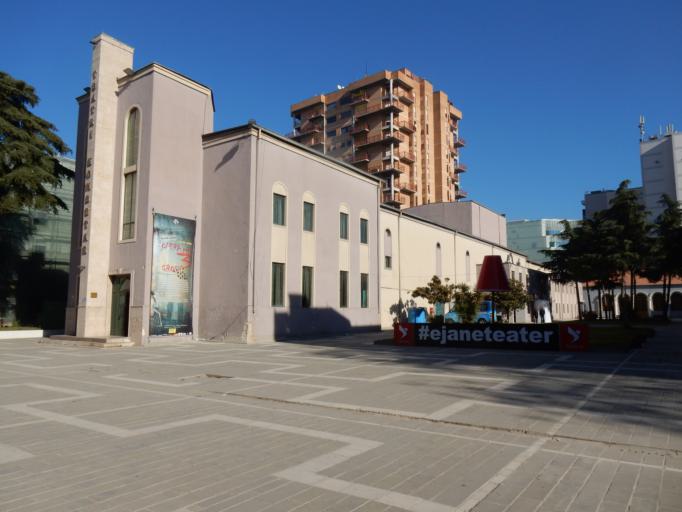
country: AL
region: Tirane
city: Tirana
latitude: 41.3263
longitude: 19.8198
